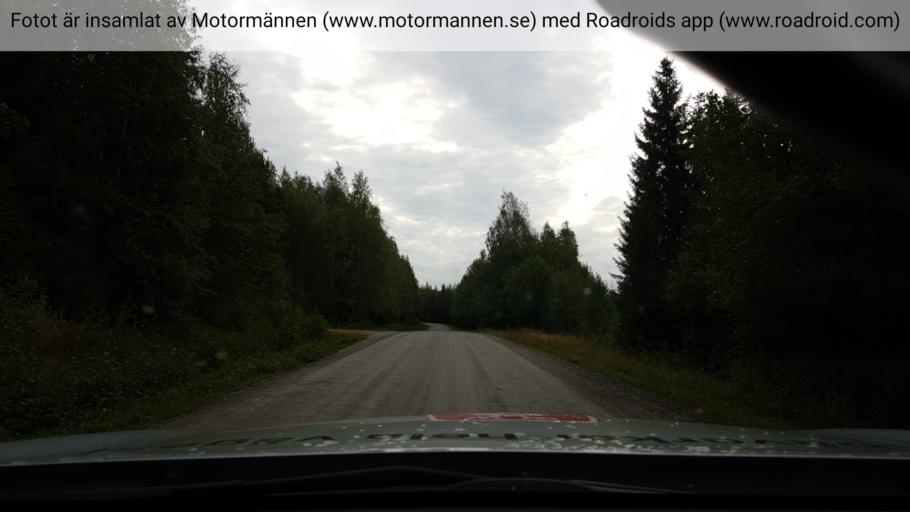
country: SE
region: Vaesterbotten
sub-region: Vannas Kommun
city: Vannasby
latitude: 64.0901
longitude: 20.0347
